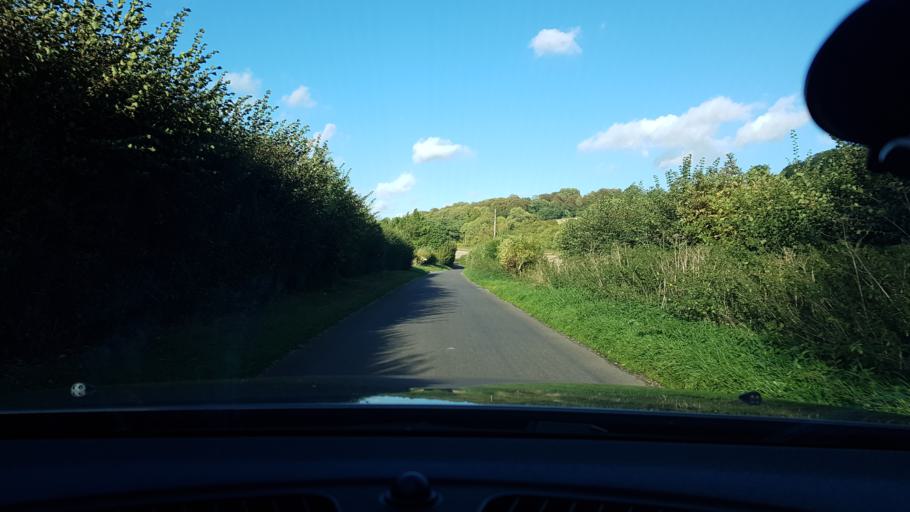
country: GB
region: England
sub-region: Wiltshire
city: Ramsbury
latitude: 51.4533
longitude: -1.5776
